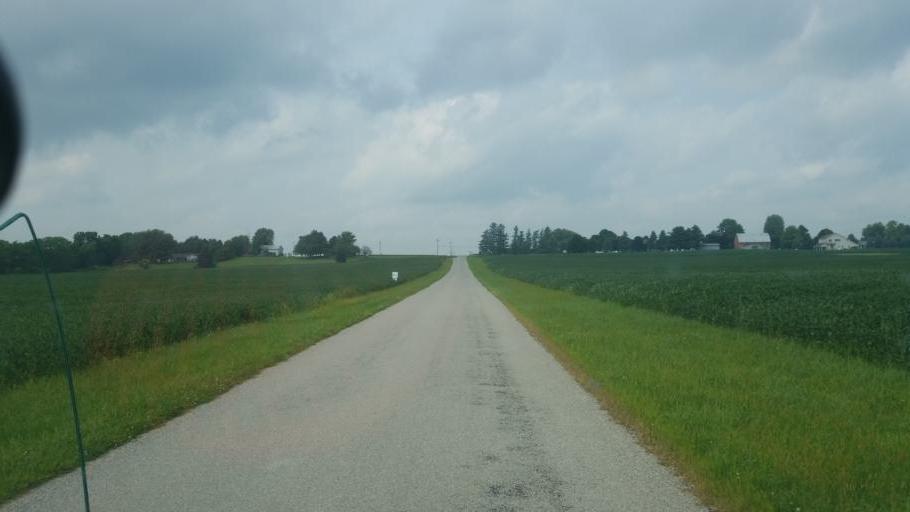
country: US
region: Ohio
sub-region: Huron County
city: New London
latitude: 41.0861
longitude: -82.4621
